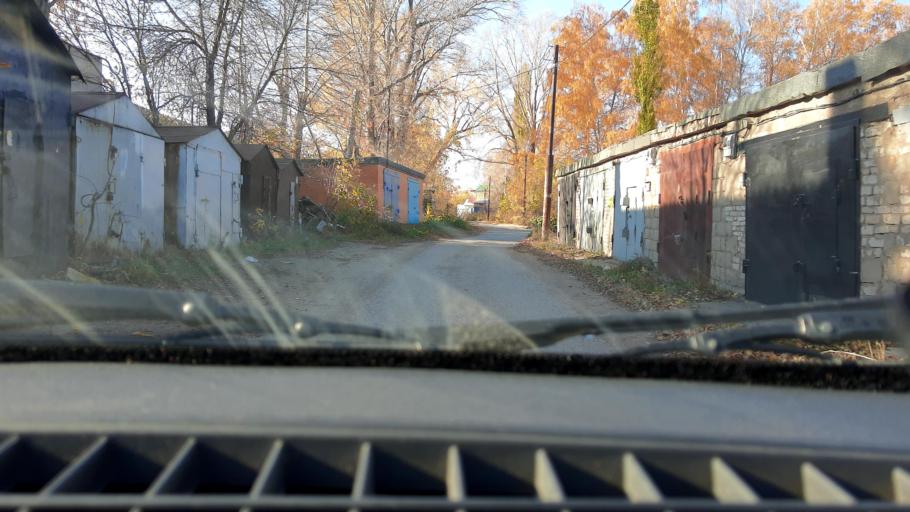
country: RU
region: Bashkortostan
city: Ufa
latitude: 54.8364
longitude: 56.1196
